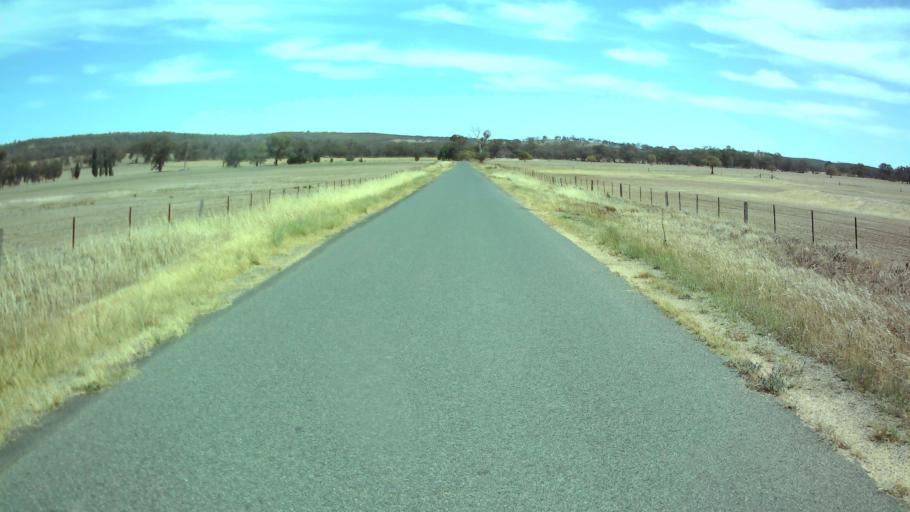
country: AU
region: New South Wales
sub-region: Weddin
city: Grenfell
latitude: -33.8388
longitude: 148.1771
